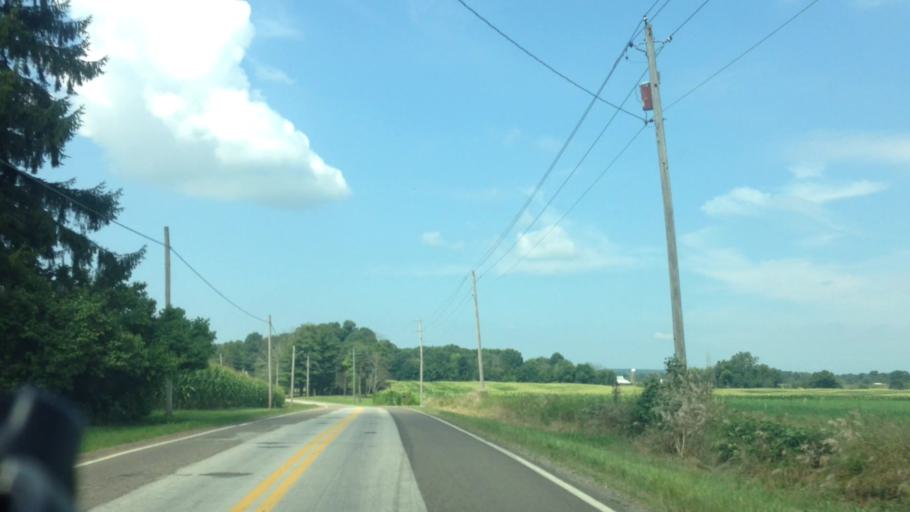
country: US
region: Ohio
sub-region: Wayne County
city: Orrville
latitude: 40.8738
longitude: -81.7474
